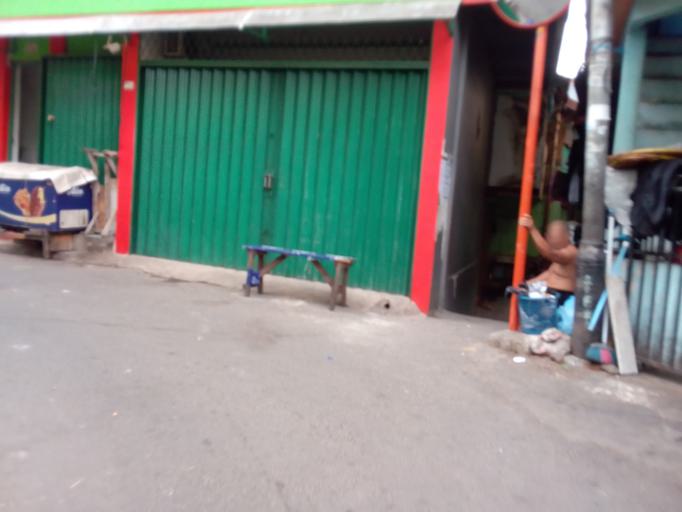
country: ID
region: Jakarta Raya
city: Jakarta
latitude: -6.1916
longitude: 106.8087
